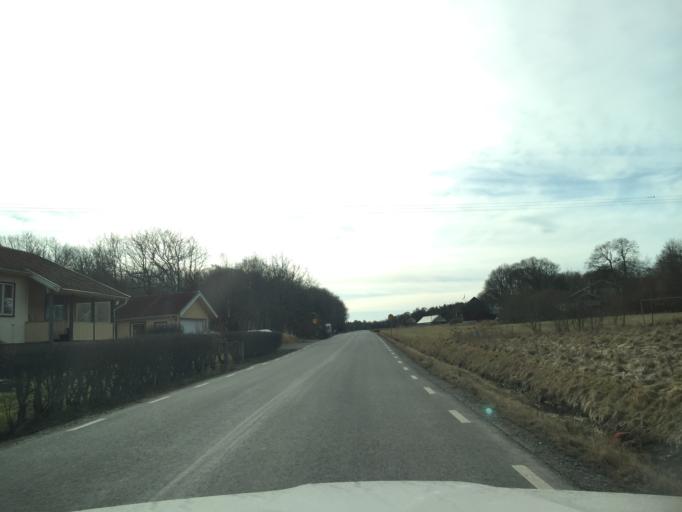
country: SE
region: Vaestra Goetaland
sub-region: Tjorns Kommun
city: Skaerhamn
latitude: 58.0341
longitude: 11.5496
